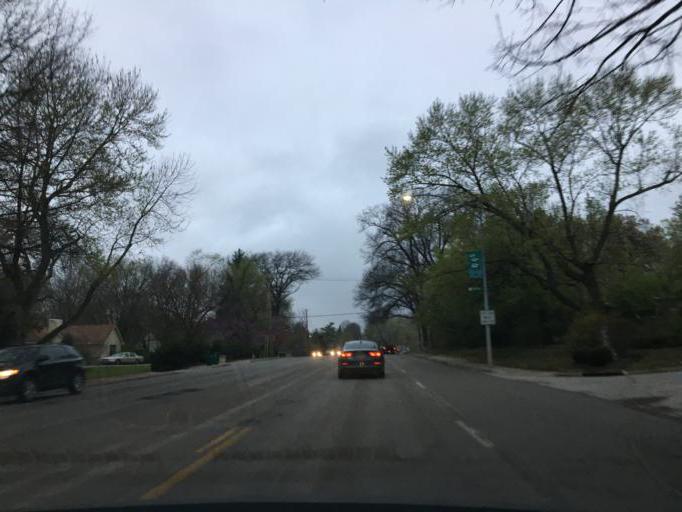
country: US
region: Kansas
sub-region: Johnson County
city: Fairway
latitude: 39.0297
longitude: -94.6295
